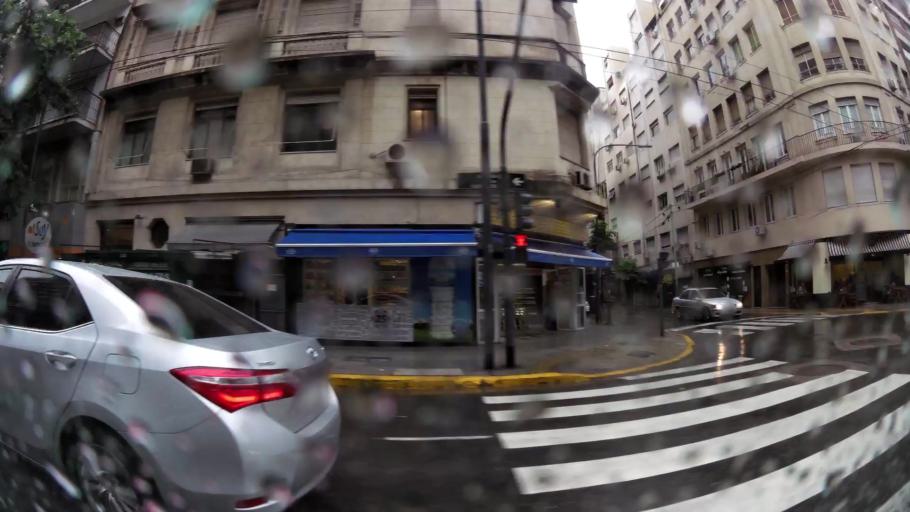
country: AR
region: Buenos Aires F.D.
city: Retiro
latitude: -34.5910
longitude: -58.3908
